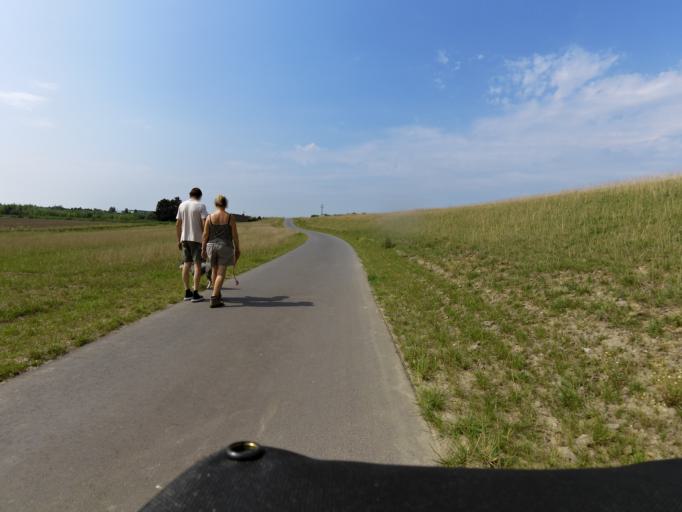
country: NL
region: South Holland
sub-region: Gemeente Binnenmaas
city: Heinenoord
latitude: 51.8299
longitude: 4.4536
